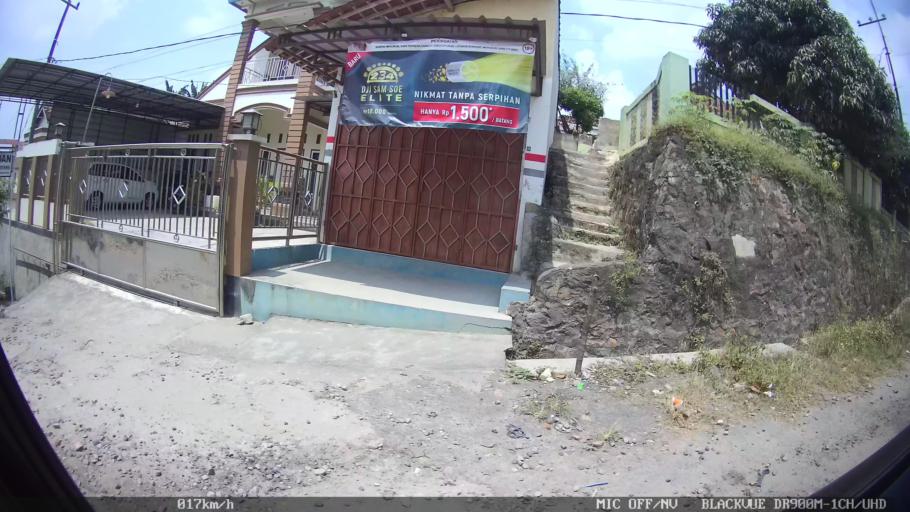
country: ID
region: Lampung
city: Pringsewu
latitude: -5.3419
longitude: 104.9864
